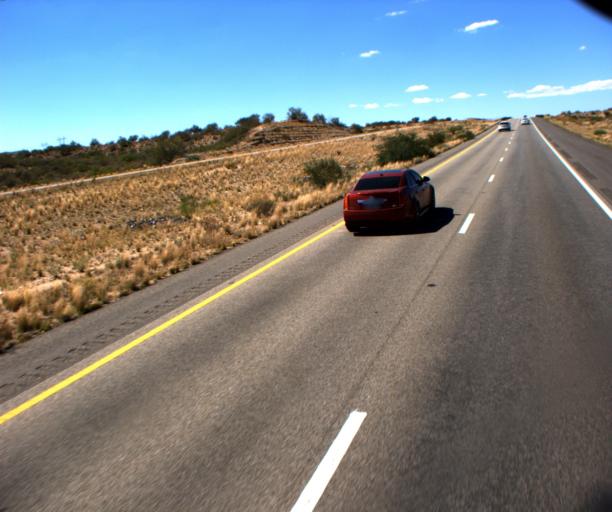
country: US
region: Arizona
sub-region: Mohave County
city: Kingman
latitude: 34.8588
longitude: -113.6405
